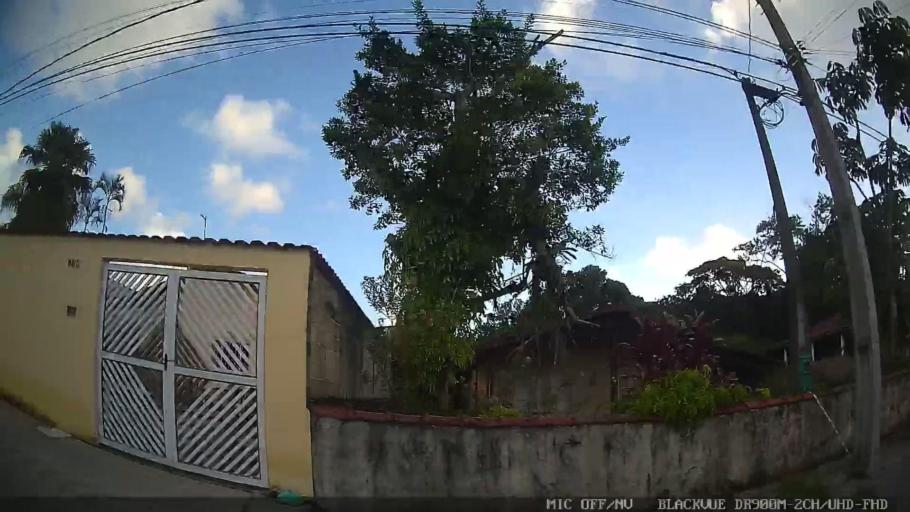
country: BR
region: Sao Paulo
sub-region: Itanhaem
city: Itanhaem
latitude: -24.1433
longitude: -46.7258
